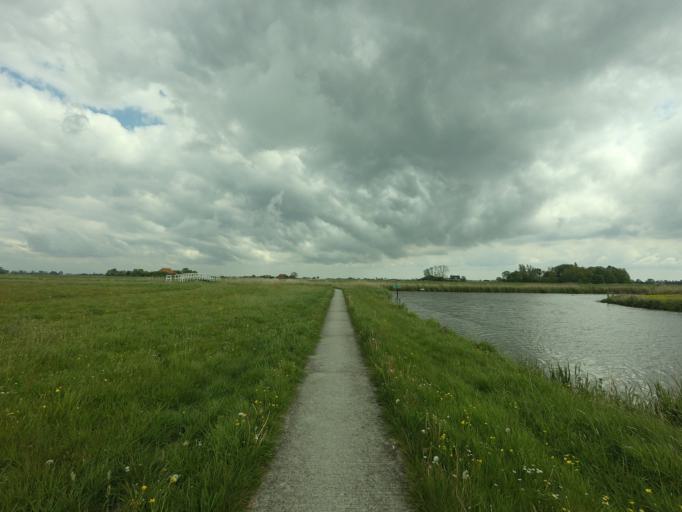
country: NL
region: Friesland
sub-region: Gemeente Littenseradiel
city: Wommels
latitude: 53.0925
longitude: 5.6309
